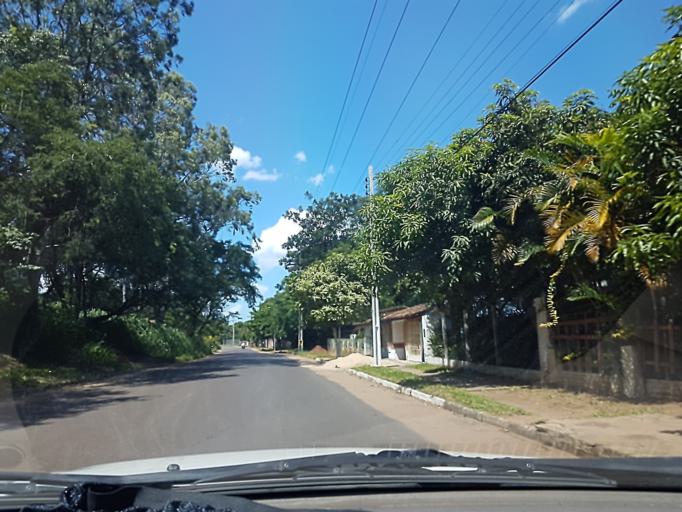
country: PY
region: Central
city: San Lorenzo
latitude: -25.2620
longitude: -57.4970
